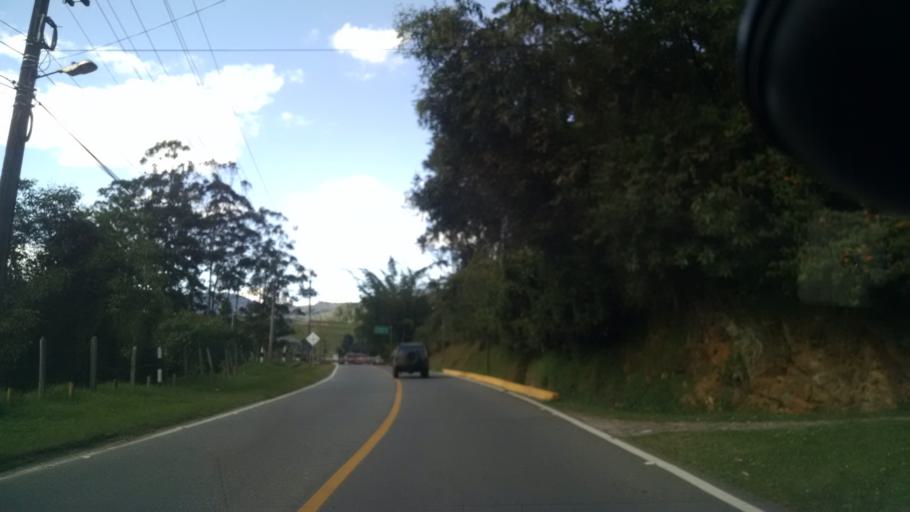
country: CO
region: Antioquia
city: El Retiro
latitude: 6.0919
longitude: -75.4896
